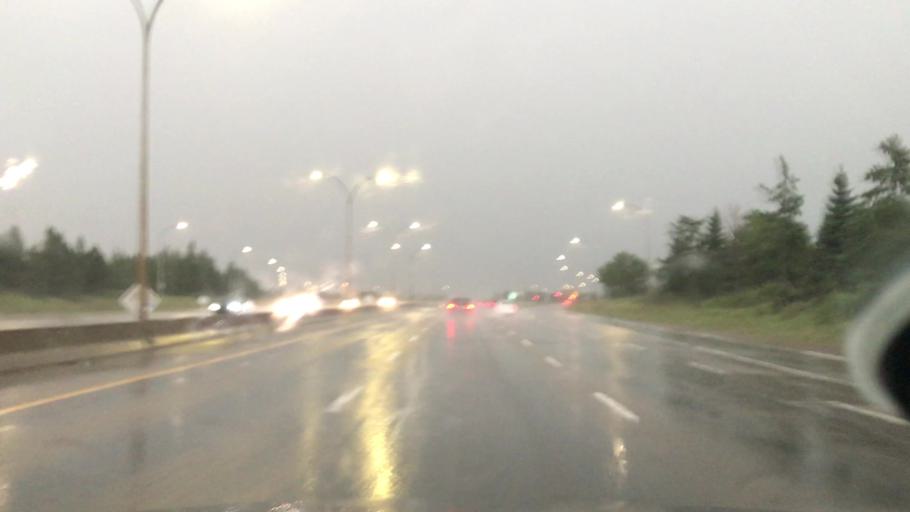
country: CA
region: Alberta
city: Edmonton
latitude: 53.4816
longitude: -113.4739
